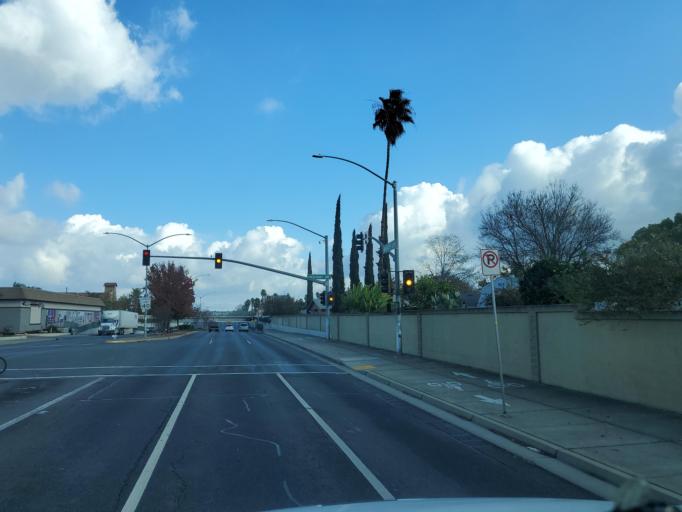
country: US
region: California
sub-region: San Joaquin County
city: Lincoln Village
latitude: 38.0005
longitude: -121.2971
